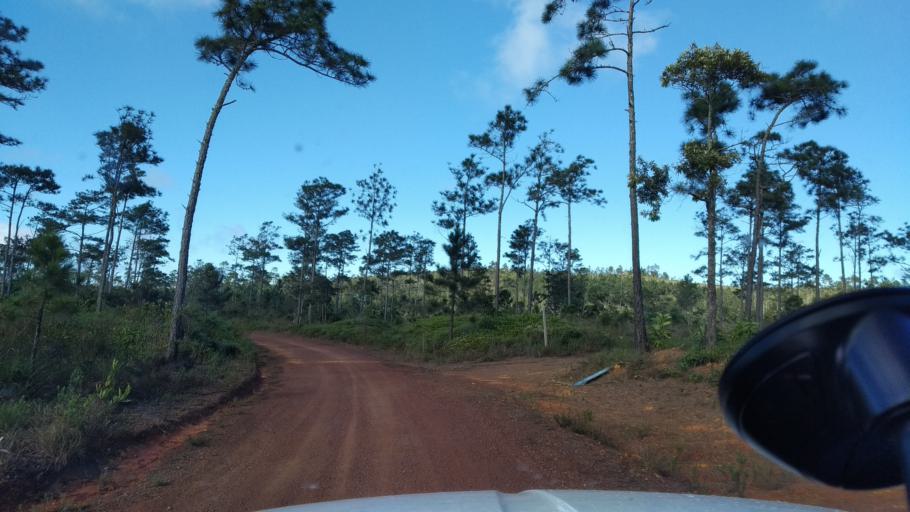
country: BZ
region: Cayo
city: Belmopan
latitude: 16.9986
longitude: -88.8406
